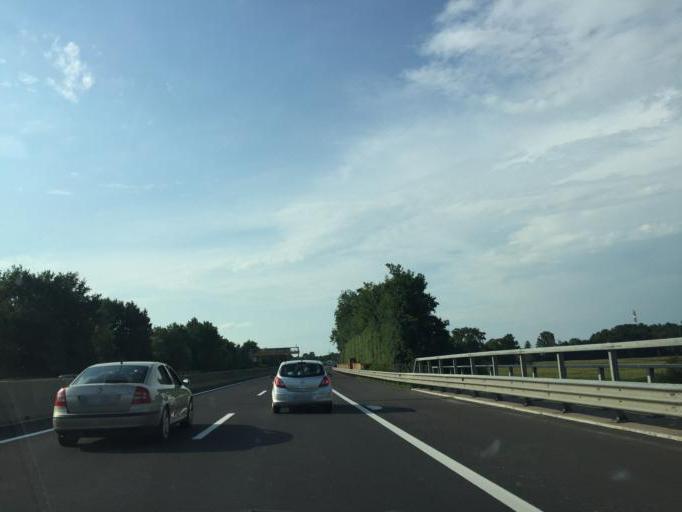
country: AT
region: Styria
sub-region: Politischer Bezirk Leibnitz
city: Weitendorf
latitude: 46.8856
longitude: 15.4735
